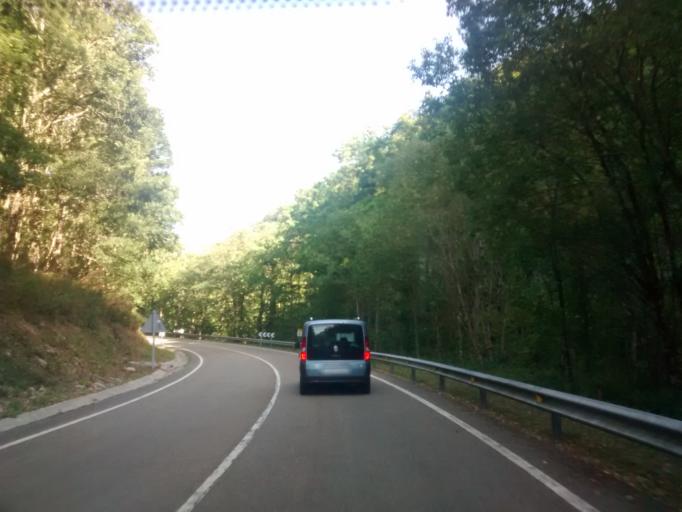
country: ES
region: Cantabria
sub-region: Provincia de Cantabria
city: Ruente
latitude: 43.1528
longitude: -4.2312
